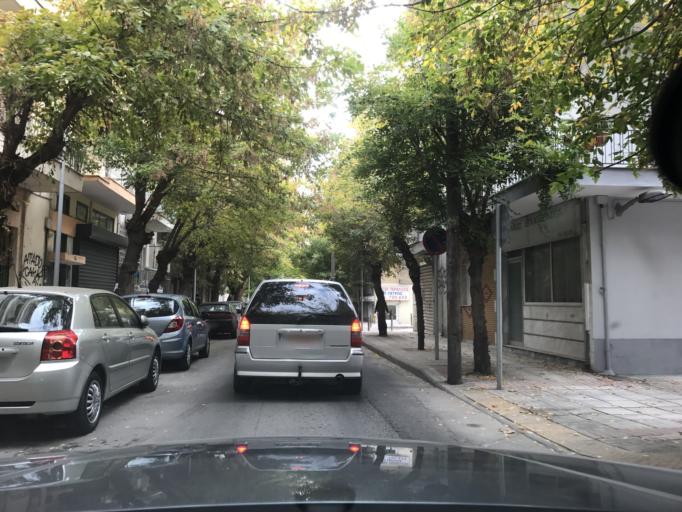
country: GR
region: Central Macedonia
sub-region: Nomos Thessalonikis
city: Ampelokipoi
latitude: 40.6484
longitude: 22.9253
